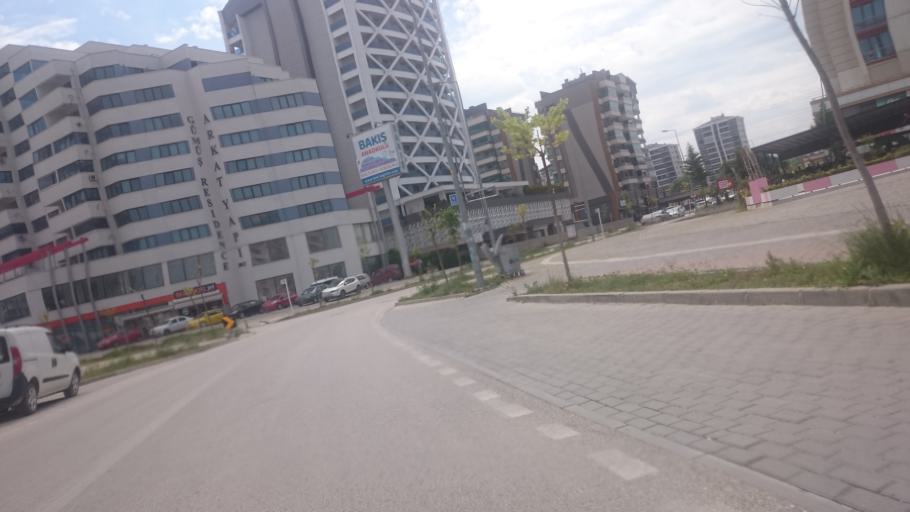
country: TR
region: Bursa
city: Cali
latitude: 40.2199
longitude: 28.9451
